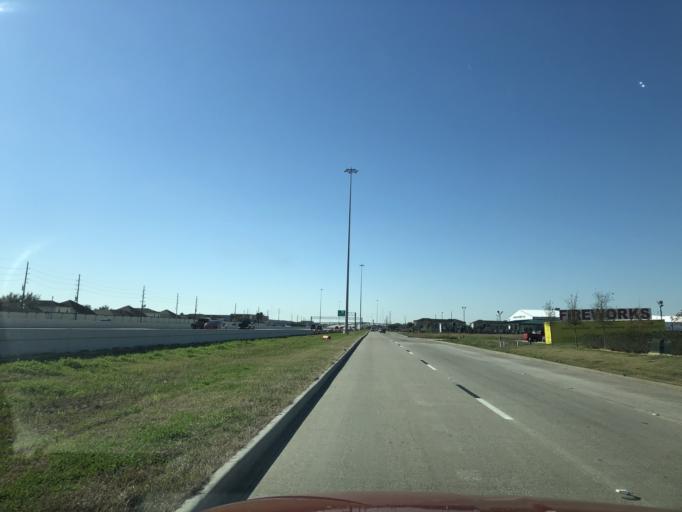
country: US
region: Texas
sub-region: Brazoria County
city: Brookside Village
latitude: 29.5985
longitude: -95.3583
